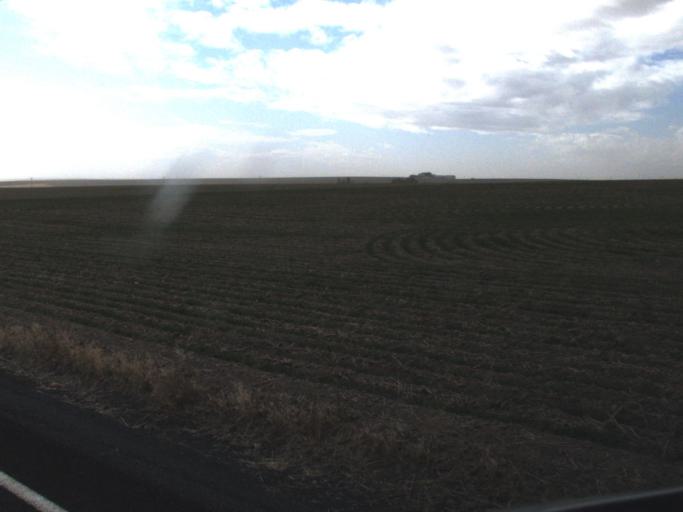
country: US
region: Washington
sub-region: Okanogan County
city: Coulee Dam
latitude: 47.8359
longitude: -118.7186
